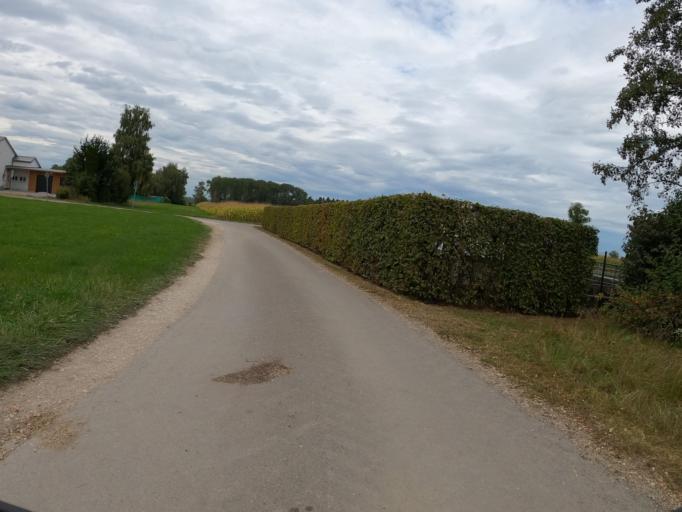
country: DE
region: Bavaria
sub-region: Swabia
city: Holzheim
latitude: 48.3890
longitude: 10.0762
